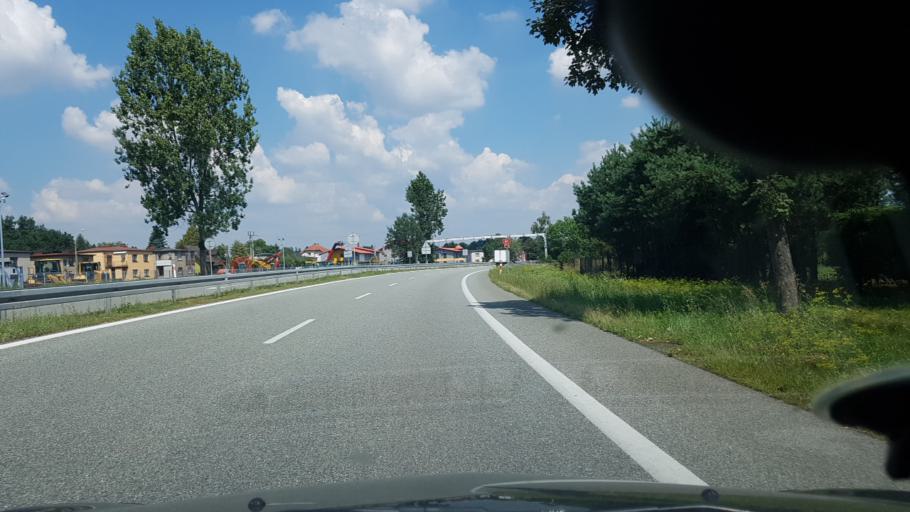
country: PL
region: Silesian Voivodeship
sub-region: Powiat pszczynski
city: Rudziczka
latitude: 50.0849
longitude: 18.7542
